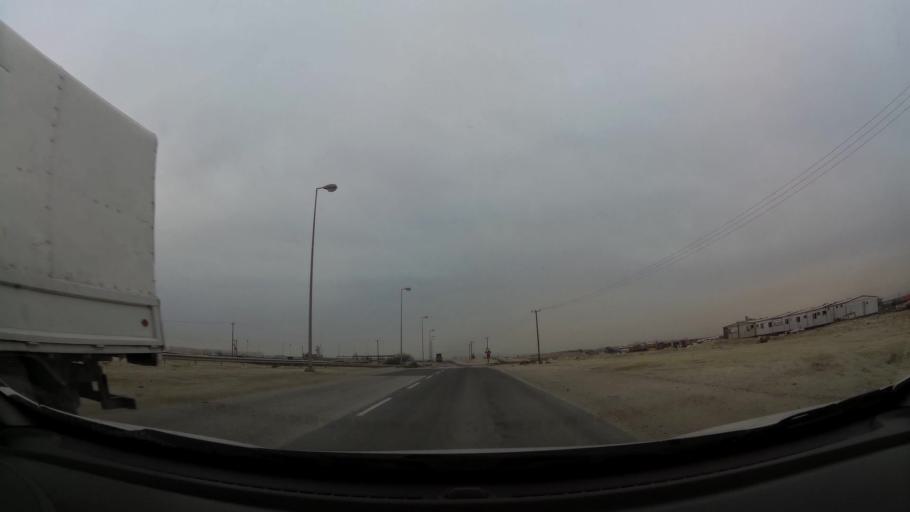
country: BH
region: Northern
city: Ar Rifa'
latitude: 26.0921
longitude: 50.5869
